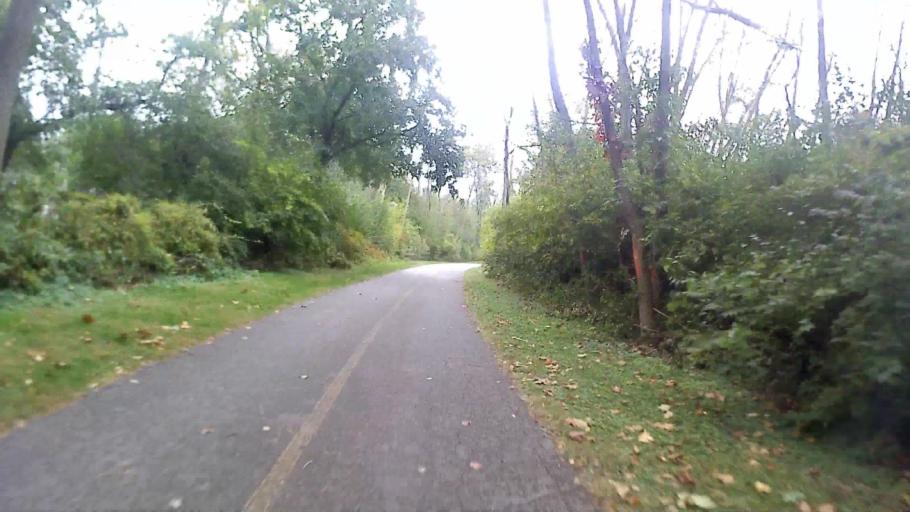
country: US
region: Illinois
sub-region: Kane County
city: Montgomery
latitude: 41.7478
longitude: -88.3638
